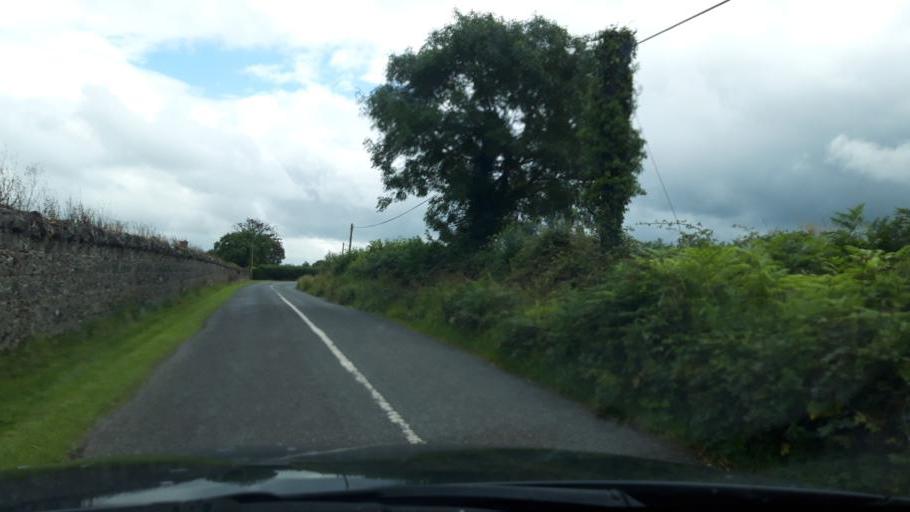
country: IE
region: Munster
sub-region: County Cork
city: Castlemartyr
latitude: 52.1353
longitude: -8.0136
